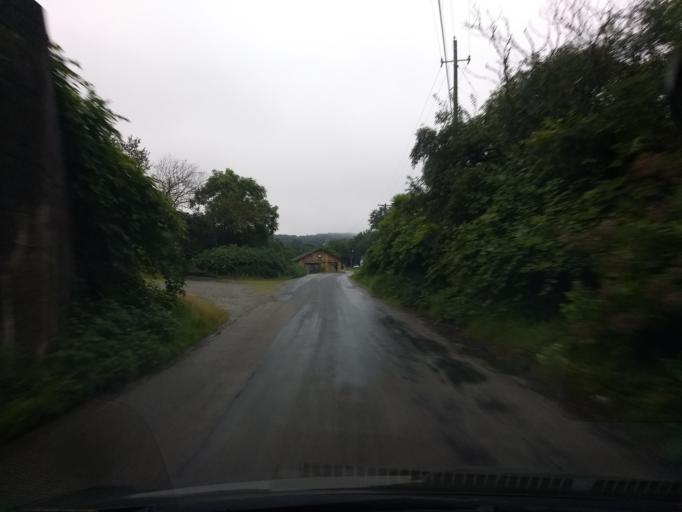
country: US
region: Pennsylvania
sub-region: Westmoreland County
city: Greensburg
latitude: 40.3510
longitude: -79.5186
